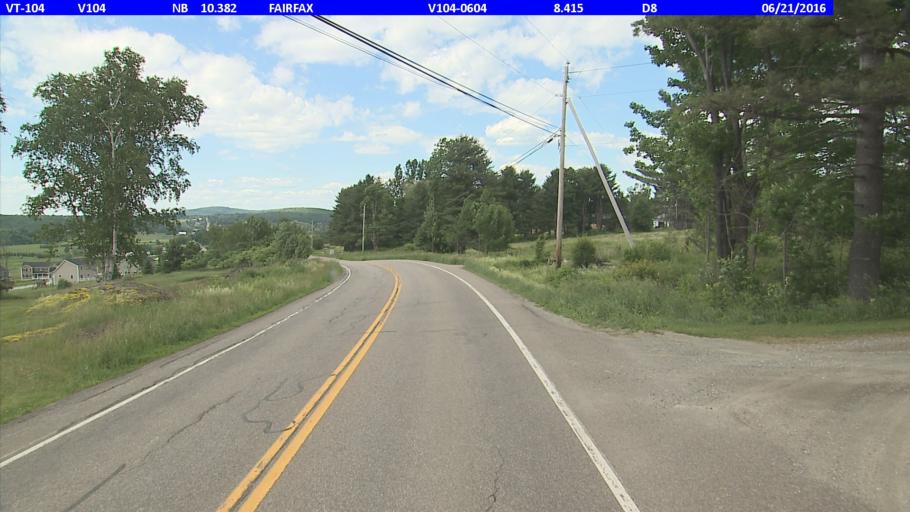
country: US
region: Vermont
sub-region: Chittenden County
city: Milton
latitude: 44.7058
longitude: -73.0364
